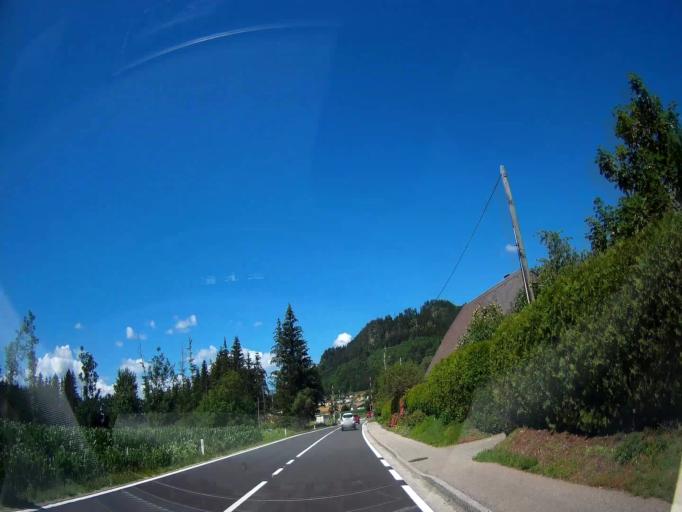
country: AT
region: Carinthia
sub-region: Politischer Bezirk Sankt Veit an der Glan
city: St. Georgen am Laengsee
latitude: 46.7647
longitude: 14.4469
